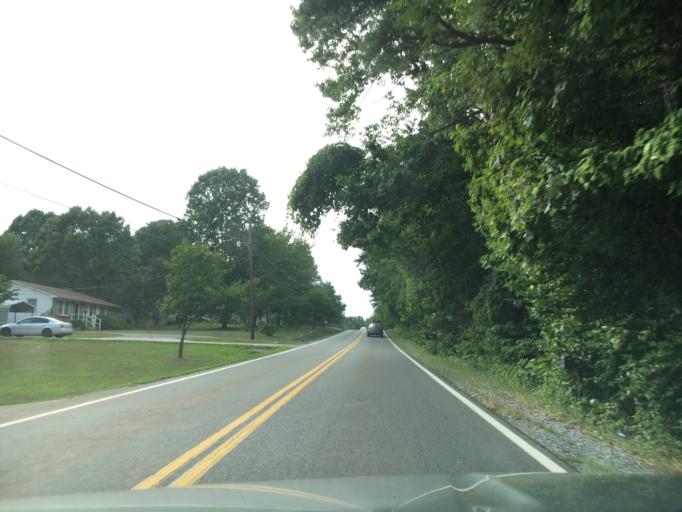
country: US
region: Virginia
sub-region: Campbell County
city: Rustburg
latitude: 37.2577
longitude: -79.1415
